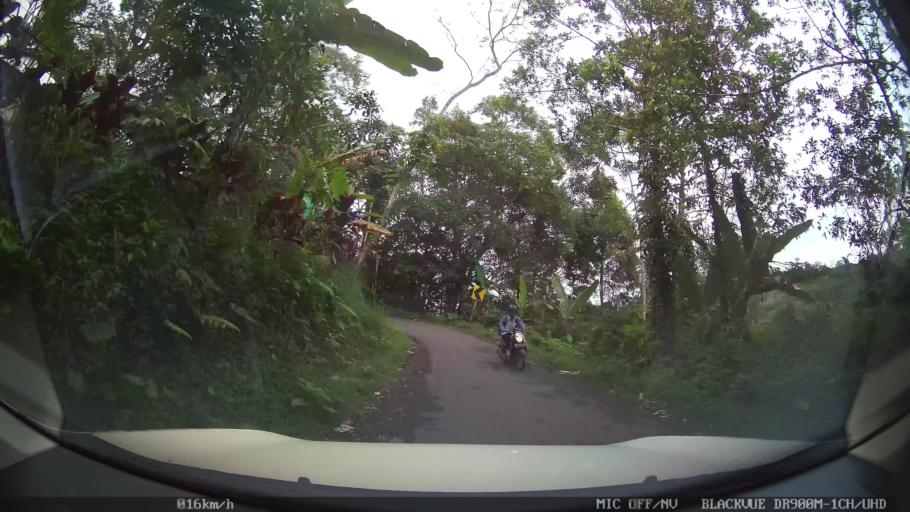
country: ID
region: Bali
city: Peneng
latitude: -8.3234
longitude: 115.1872
